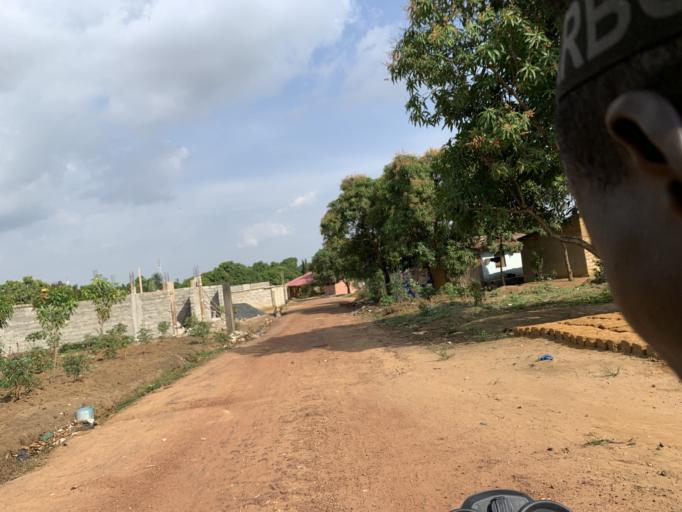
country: SL
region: Western Area
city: Waterloo
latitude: 8.3412
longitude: -13.0462
